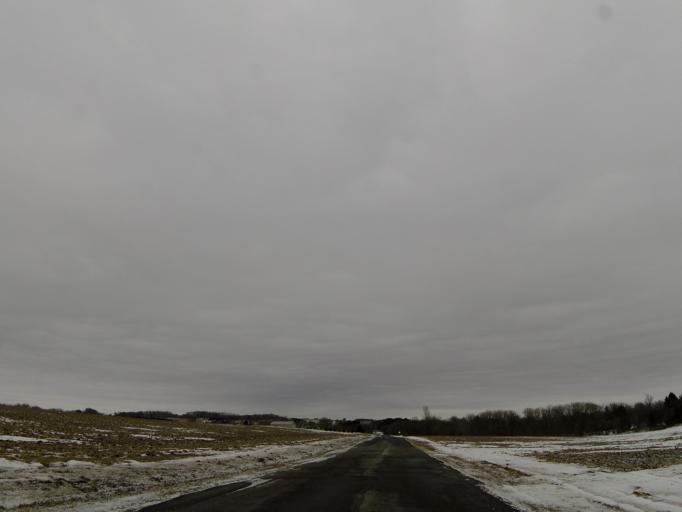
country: US
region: Minnesota
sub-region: Dakota County
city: Hastings
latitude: 44.7998
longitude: -92.8701
